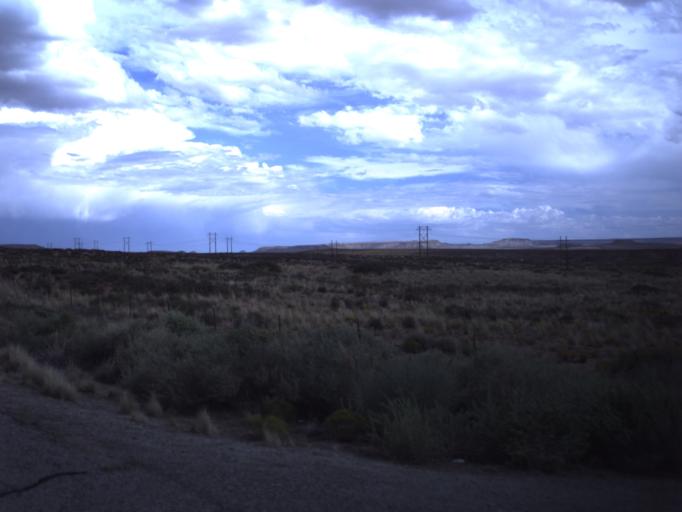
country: US
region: Utah
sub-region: San Juan County
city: Blanding
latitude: 37.3014
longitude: -109.4441
